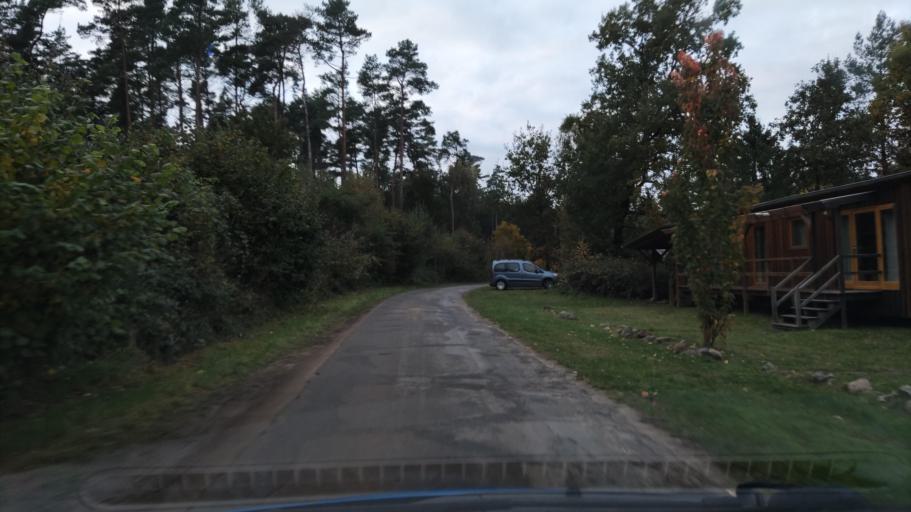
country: DE
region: Lower Saxony
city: Karwitz
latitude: 53.1281
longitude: 10.9917
